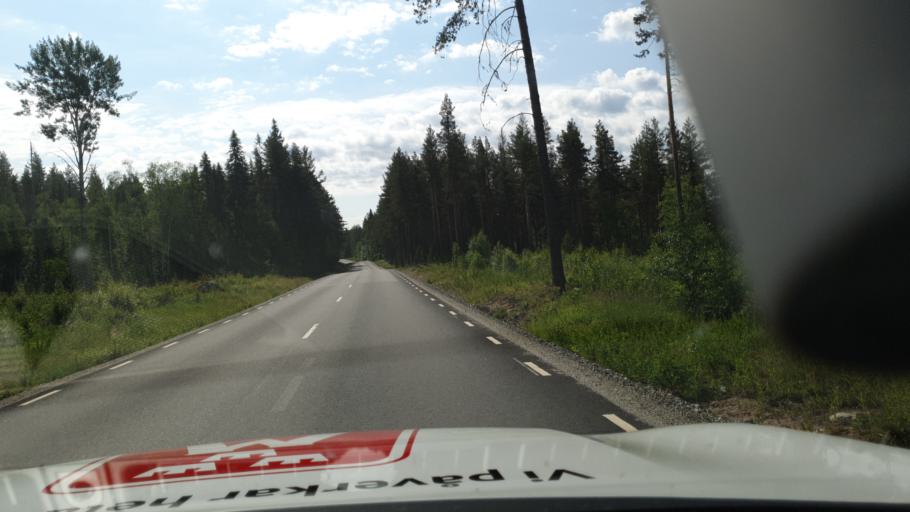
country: SE
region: Vaesterbotten
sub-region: Norsjo Kommun
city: Norsjoe
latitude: 64.6508
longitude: 19.2770
